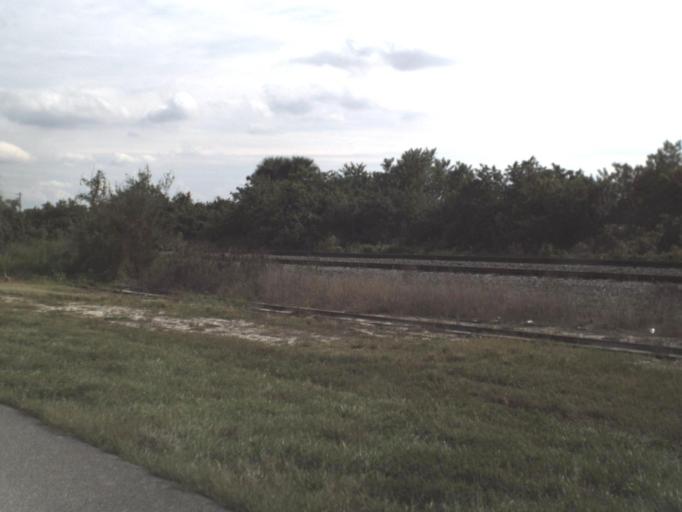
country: US
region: Florida
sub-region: Okeechobee County
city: Taylor Creek
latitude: 27.2096
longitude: -80.7539
